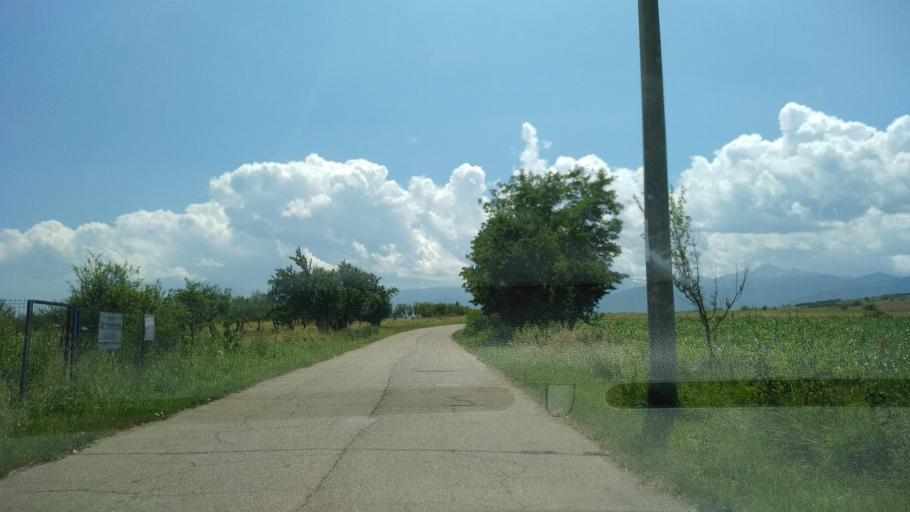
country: RO
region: Hunedoara
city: Densus
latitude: 45.5727
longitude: 22.8098
